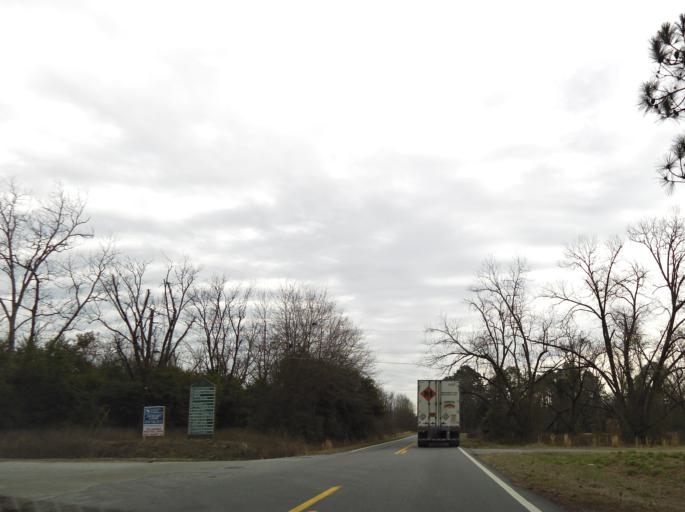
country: US
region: Georgia
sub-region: Houston County
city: Centerville
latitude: 32.6917
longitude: -83.6712
